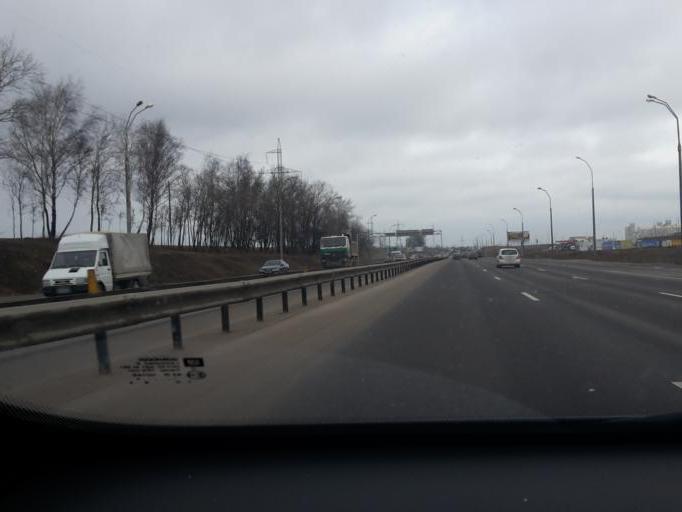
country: BY
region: Minsk
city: Zhdanovichy
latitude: 53.9126
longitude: 27.4104
